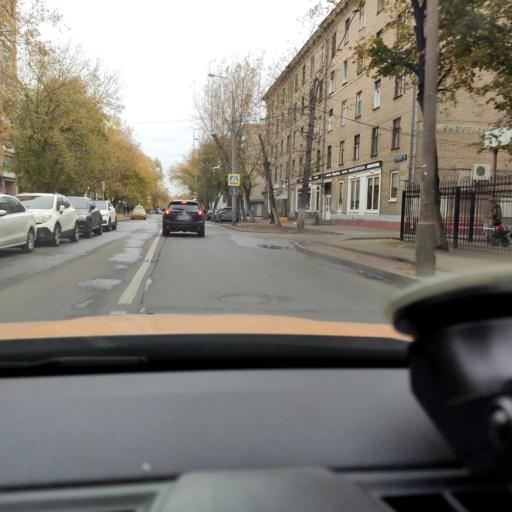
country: RU
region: Moscow
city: Tekstil'shchiki
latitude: 55.7035
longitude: 37.7433
